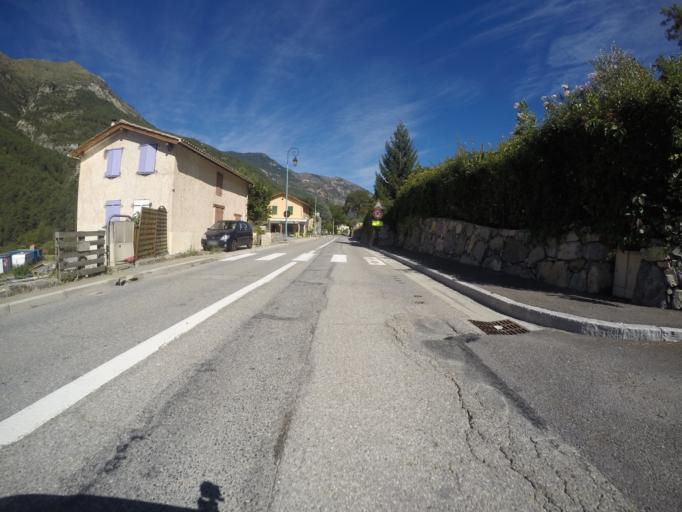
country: FR
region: Provence-Alpes-Cote d'Azur
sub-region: Departement des Alpes-Maritimes
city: Gilette
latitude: 43.9611
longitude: 7.1547
